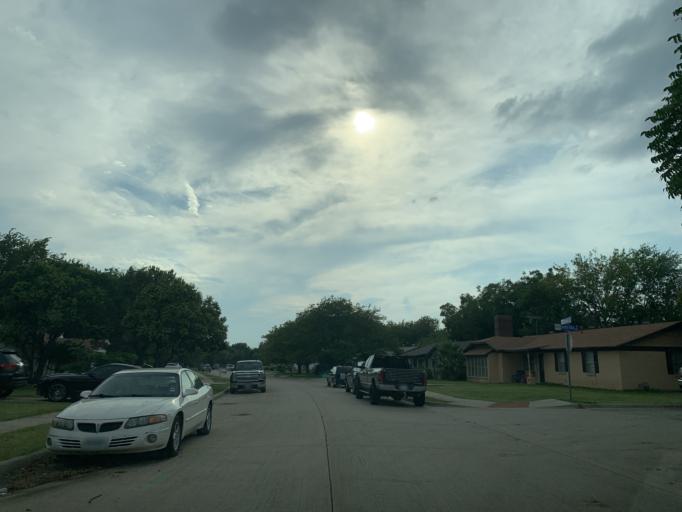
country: US
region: Texas
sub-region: Tarrant County
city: Watauga
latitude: 32.8623
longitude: -97.2387
